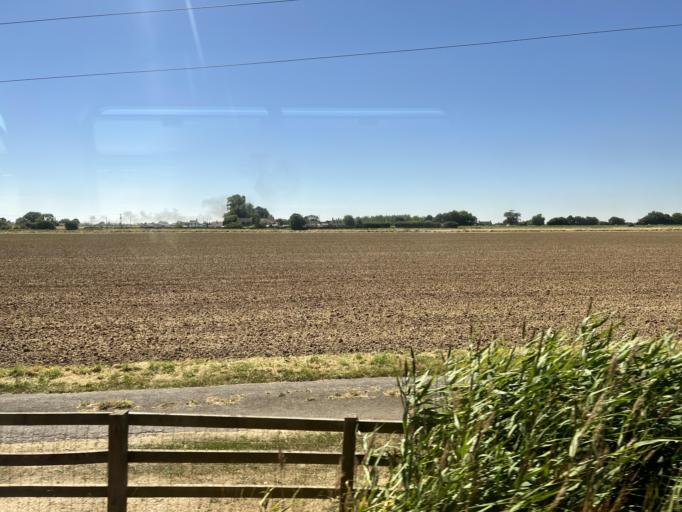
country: GB
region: England
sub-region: Lincolnshire
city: Wainfleet All Saints
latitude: 53.1099
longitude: 0.2243
